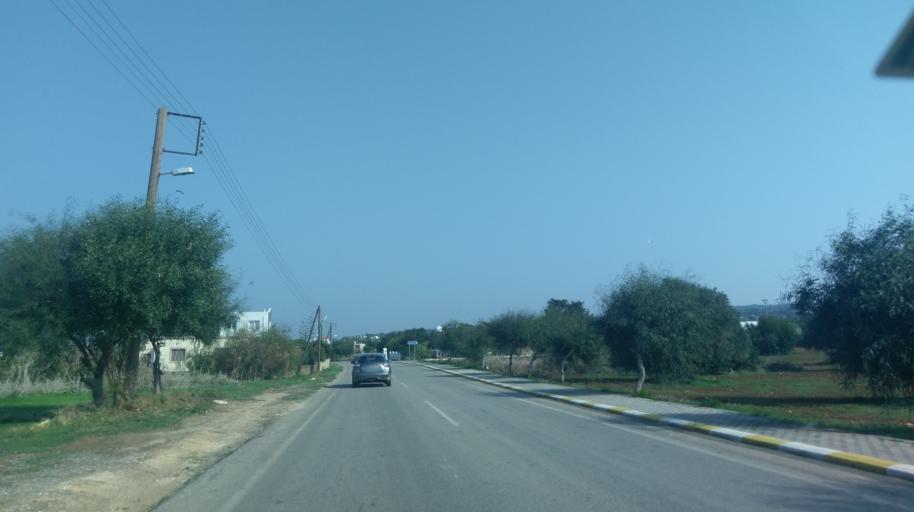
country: CY
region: Ammochostos
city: Leonarisso
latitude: 35.5253
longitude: 34.1783
